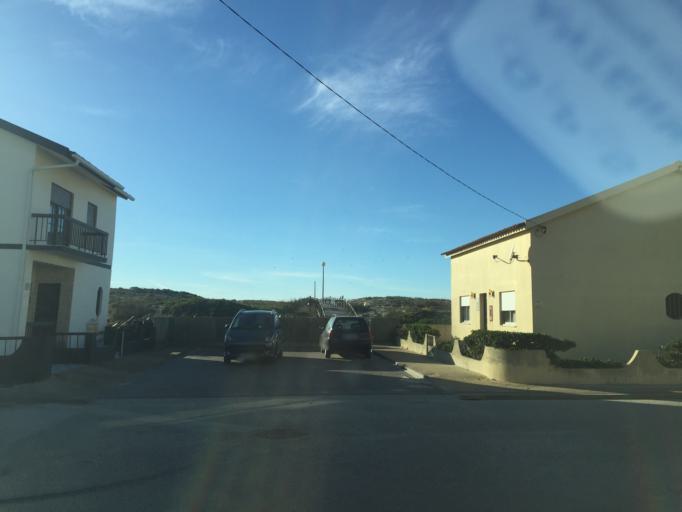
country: PT
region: Coimbra
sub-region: Figueira da Foz
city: Lavos
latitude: 40.0883
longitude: -8.8753
